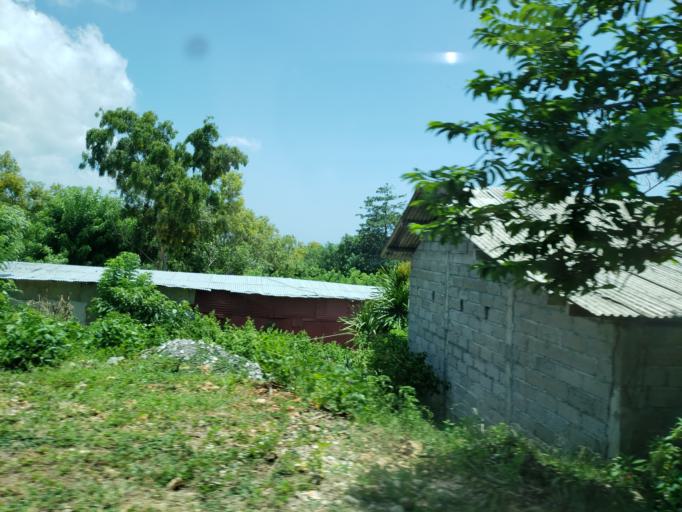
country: ID
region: Bali
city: Kangin
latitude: -8.8416
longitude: 115.1404
